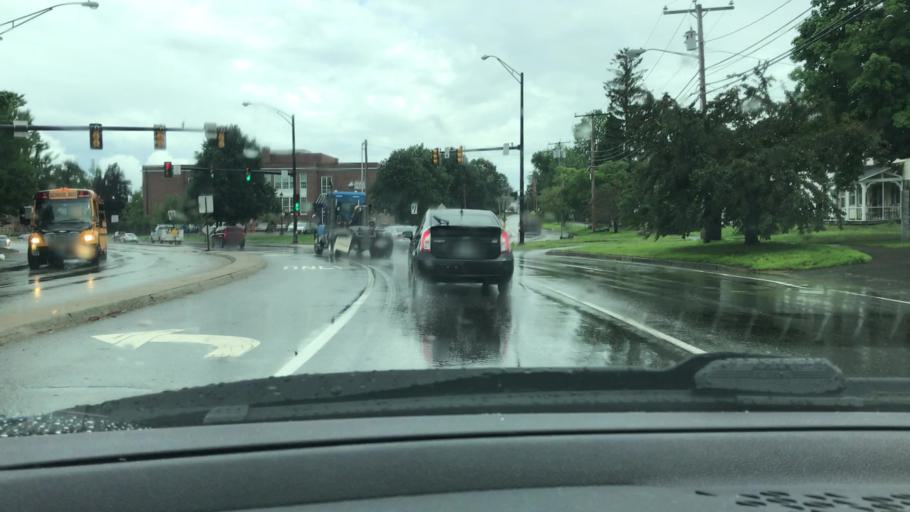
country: US
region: New Hampshire
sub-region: Merrimack County
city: Concord
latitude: 43.2159
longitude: -71.5441
